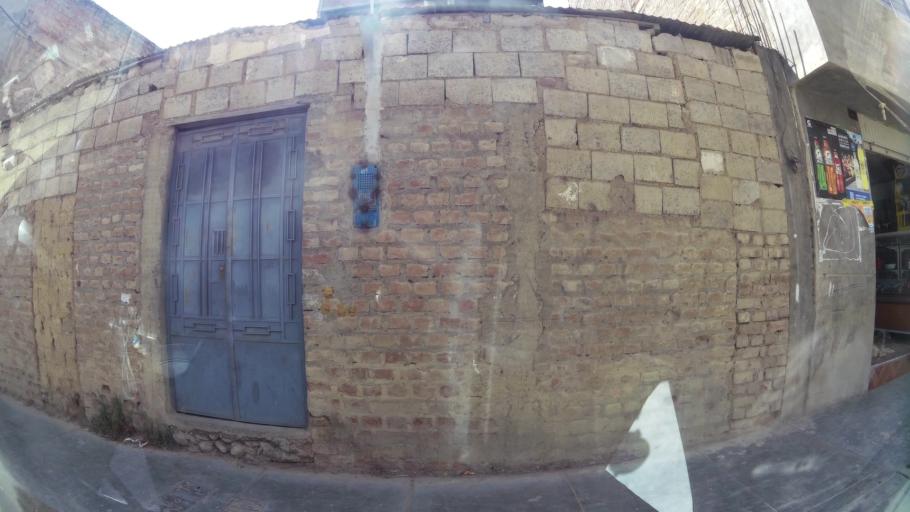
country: PE
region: Junin
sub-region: Provincia de Huancayo
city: Huancayo
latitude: -12.0667
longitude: -75.1989
